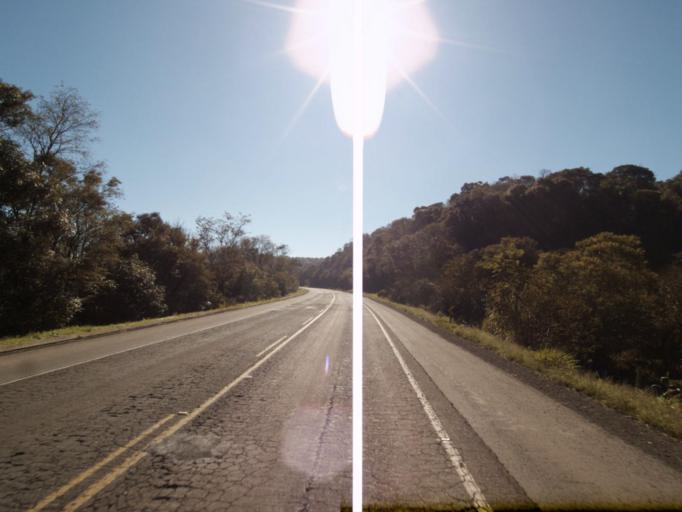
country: BR
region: Rio Grande do Sul
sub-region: Frederico Westphalen
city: Frederico Westphalen
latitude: -27.0123
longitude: -53.2254
